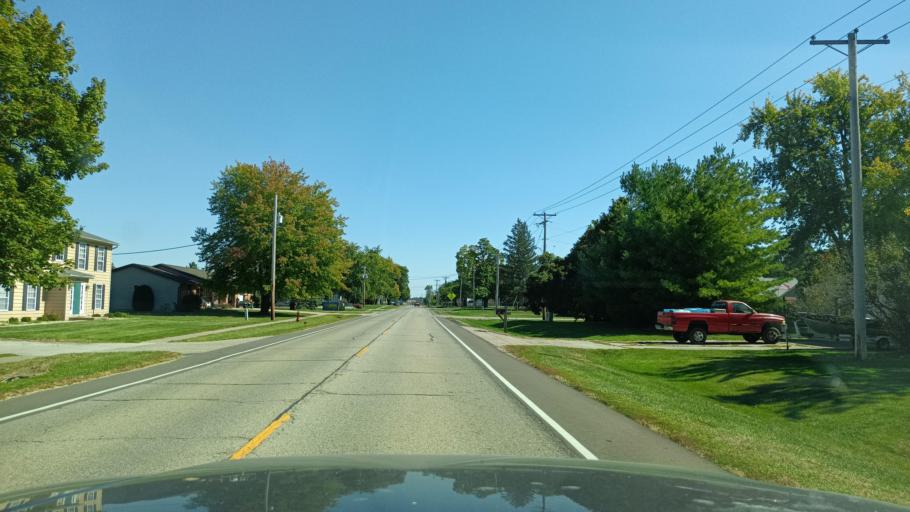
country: US
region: Illinois
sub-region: McLean County
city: Danvers
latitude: 40.6172
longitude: -89.2068
